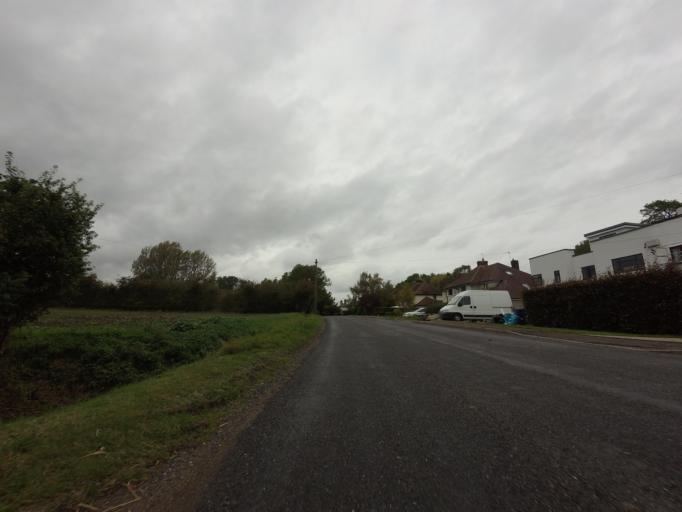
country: GB
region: England
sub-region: Cambridgeshire
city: Comberton
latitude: 52.1557
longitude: 0.0078
